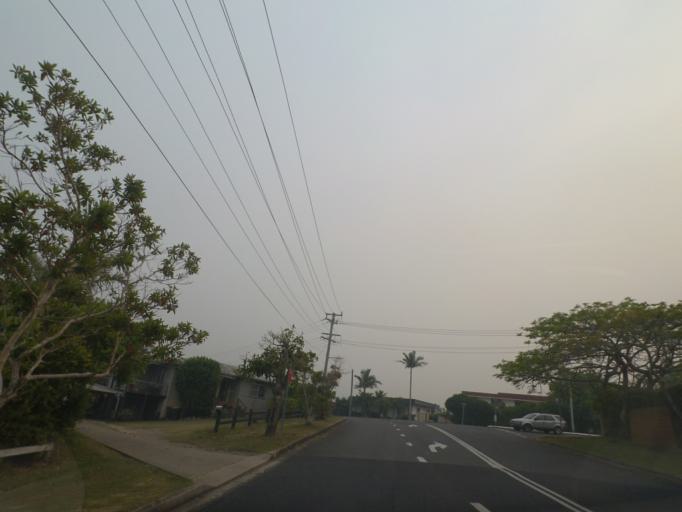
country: AU
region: New South Wales
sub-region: Coffs Harbour
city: Coffs Harbour
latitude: -30.2884
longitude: 153.1081
